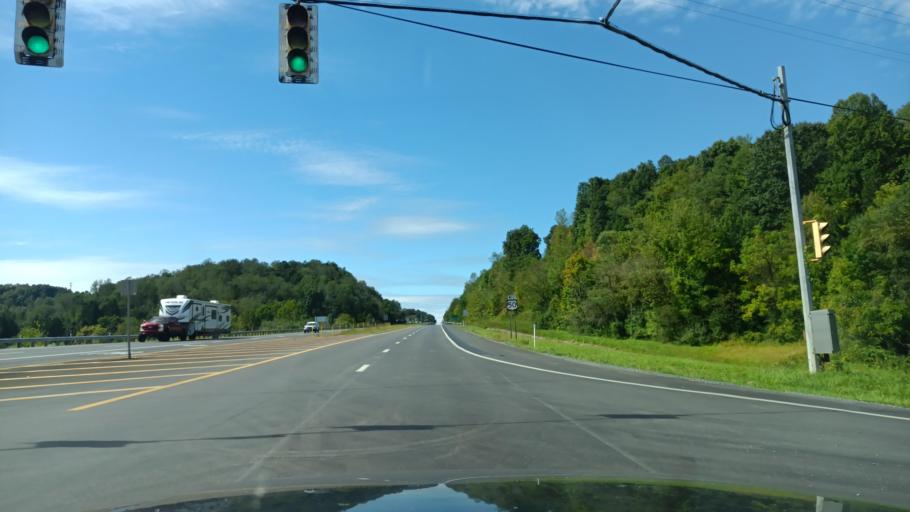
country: US
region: West Virginia
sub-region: Harrison County
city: Clarksburg
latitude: 39.2838
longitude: -80.4000
